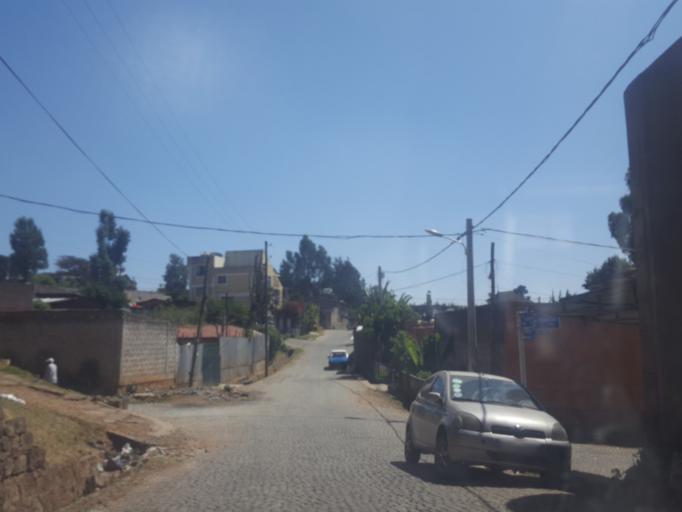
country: ET
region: Adis Abeba
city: Addis Ababa
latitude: 9.0575
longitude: 38.7240
